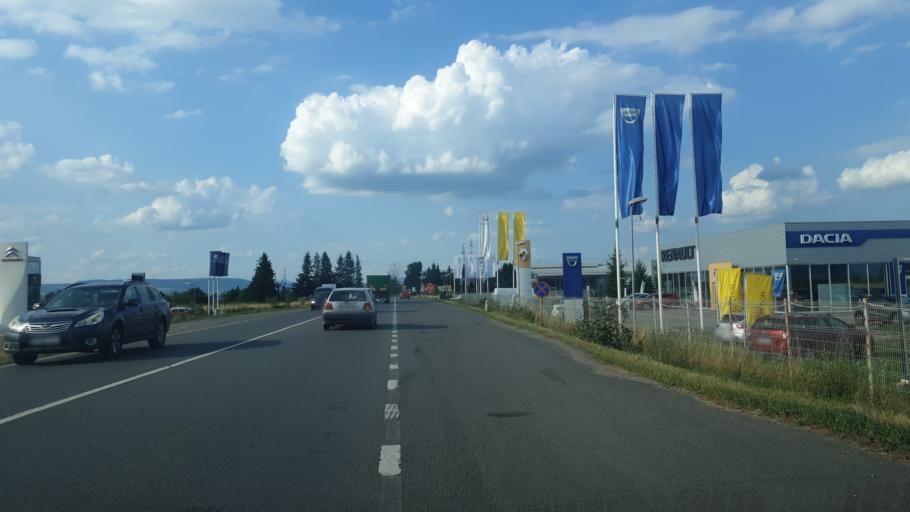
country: RO
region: Covasna
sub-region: Municipiul Sfantu Gheorghe
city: Sfantu-Gheorghe
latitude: 45.8432
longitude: 25.8038
